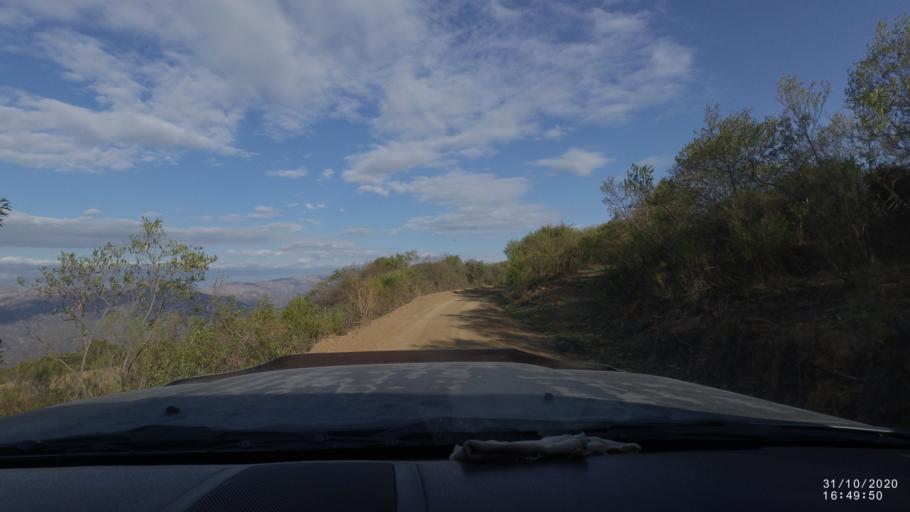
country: BO
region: Chuquisaca
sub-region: Provincia Zudanez
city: Mojocoya
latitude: -18.5074
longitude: -64.5712
